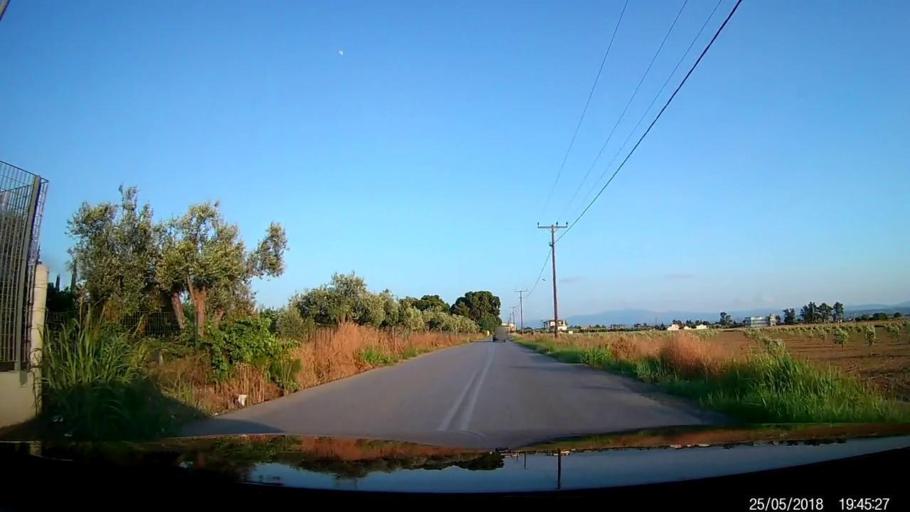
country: GR
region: Central Greece
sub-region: Nomos Evvoias
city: Ayios Nikolaos
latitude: 38.4330
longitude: 23.6332
